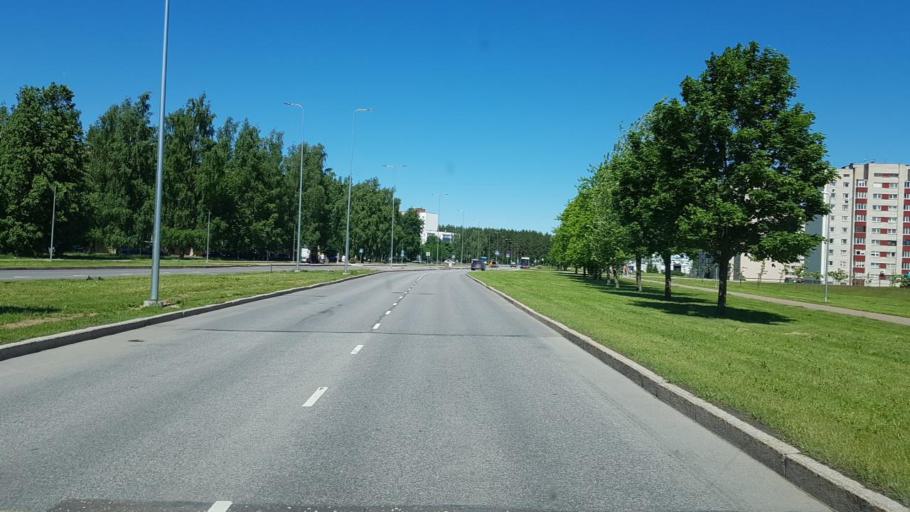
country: EE
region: Ida-Virumaa
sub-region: Narva linn
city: Narva
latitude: 59.3881
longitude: 28.1748
